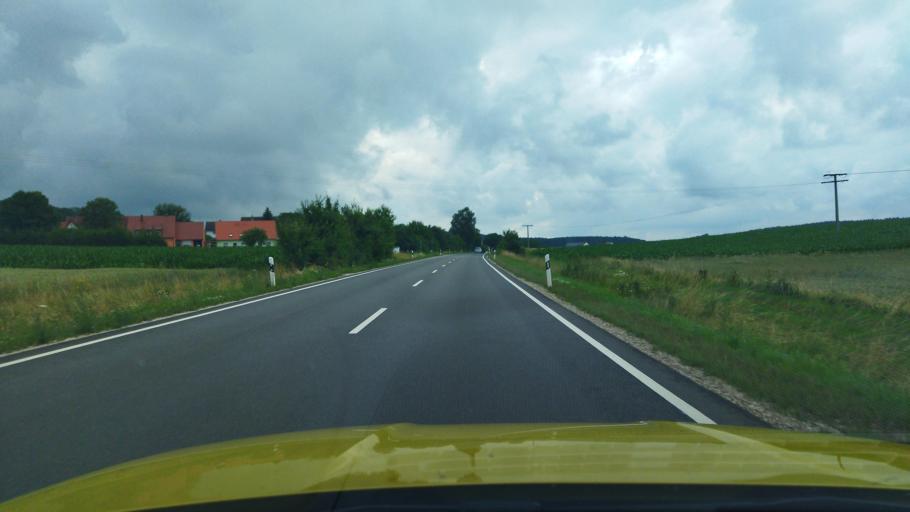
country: DE
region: Bavaria
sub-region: Regierungsbezirk Mittelfranken
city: Absberg
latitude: 49.1100
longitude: 10.8946
